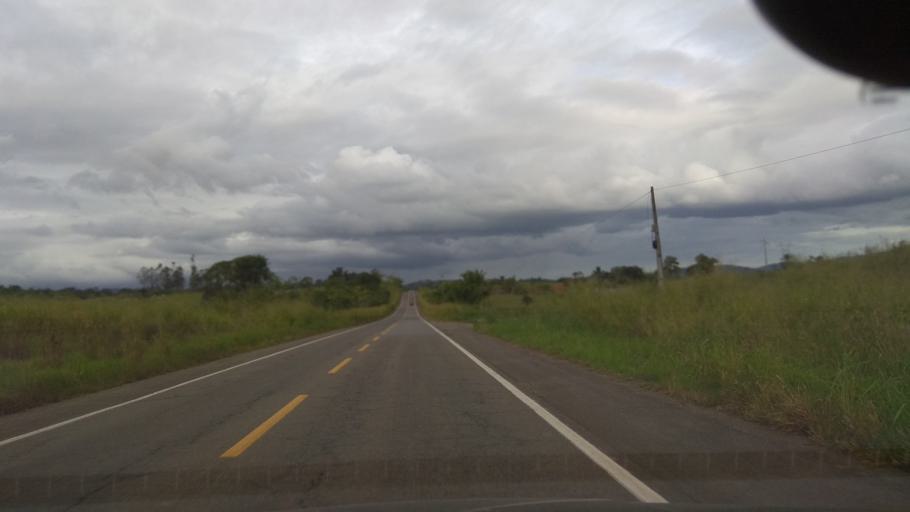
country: BR
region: Bahia
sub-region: Ipiau
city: Ipiau
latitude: -14.1944
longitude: -39.6431
